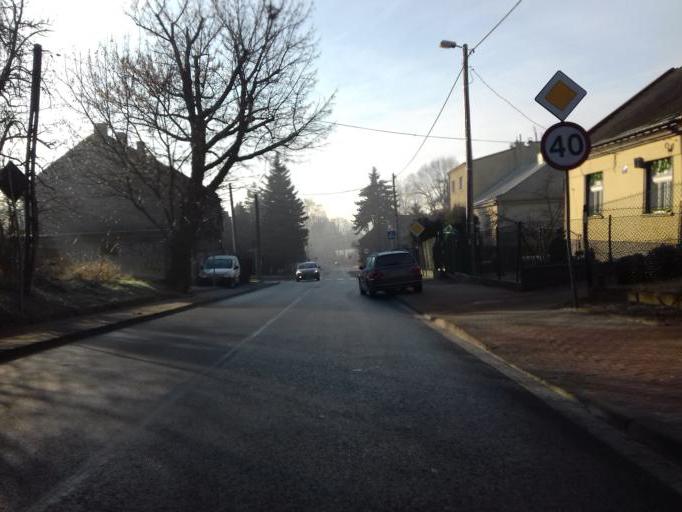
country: PL
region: Lesser Poland Voivodeship
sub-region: Krakow
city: Krakow
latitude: 50.0199
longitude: 19.9429
